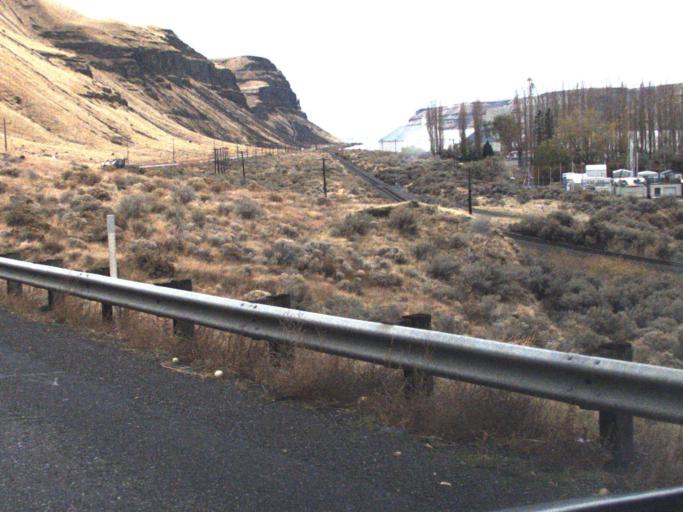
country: US
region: Washington
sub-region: Benton County
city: Finley
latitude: 46.0280
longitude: -118.9322
